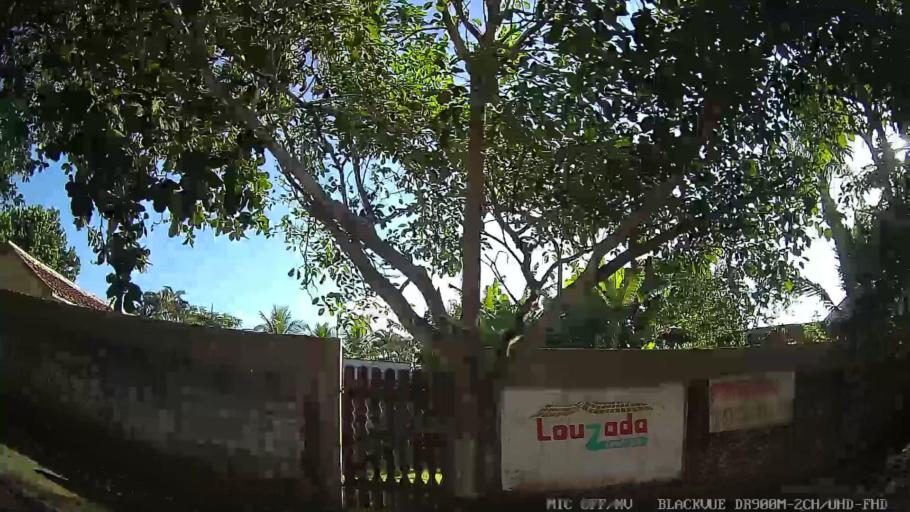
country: BR
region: Sao Paulo
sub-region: Peruibe
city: Peruibe
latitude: -24.2916
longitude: -46.9583
